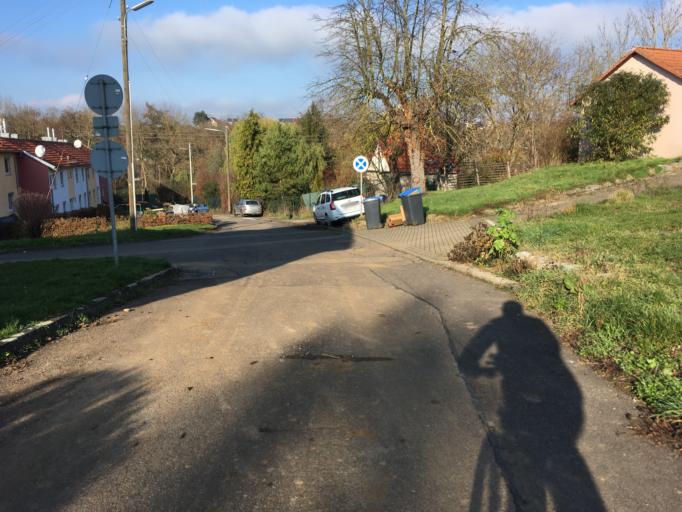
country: DE
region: Baden-Wuerttemberg
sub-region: Regierungsbezirk Stuttgart
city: Heilbronn
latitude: 49.1637
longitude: 9.1875
